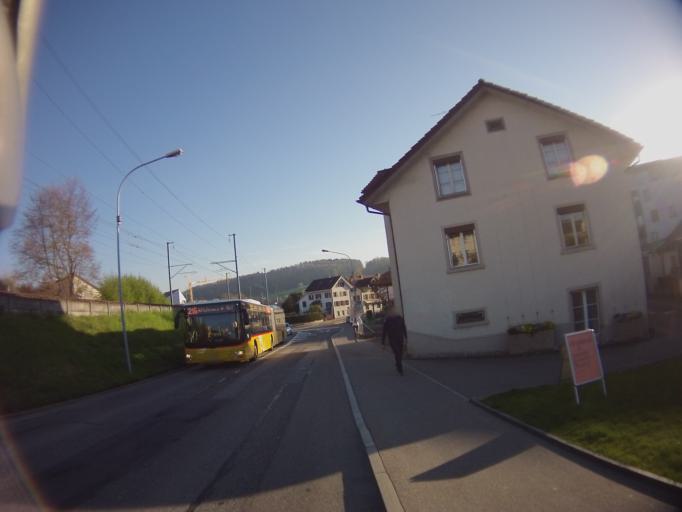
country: CH
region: Zurich
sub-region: Bezirk Affoltern
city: Affoltern / Oberdorf
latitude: 47.2795
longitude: 8.4499
